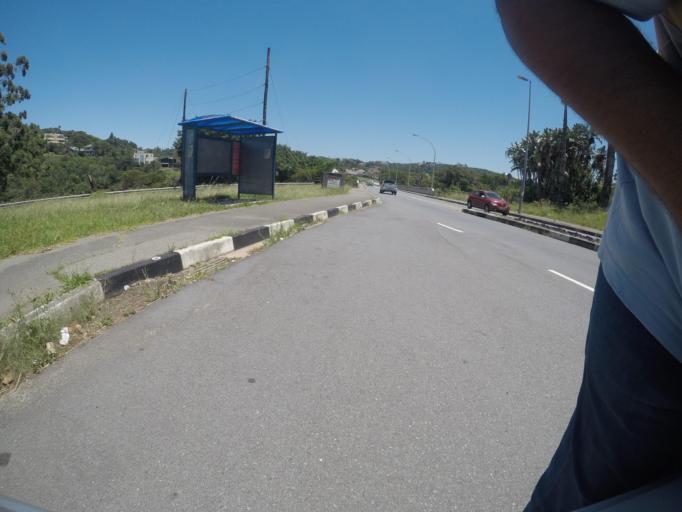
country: ZA
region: Eastern Cape
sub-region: Buffalo City Metropolitan Municipality
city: East London
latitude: -32.9737
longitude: 27.9268
